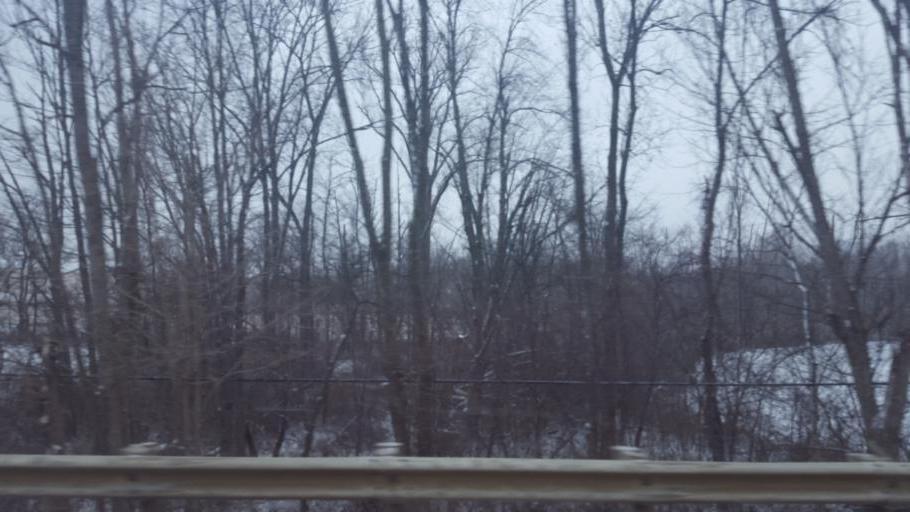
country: US
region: Ohio
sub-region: Knox County
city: Oak Hill
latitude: 40.3383
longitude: -82.1515
